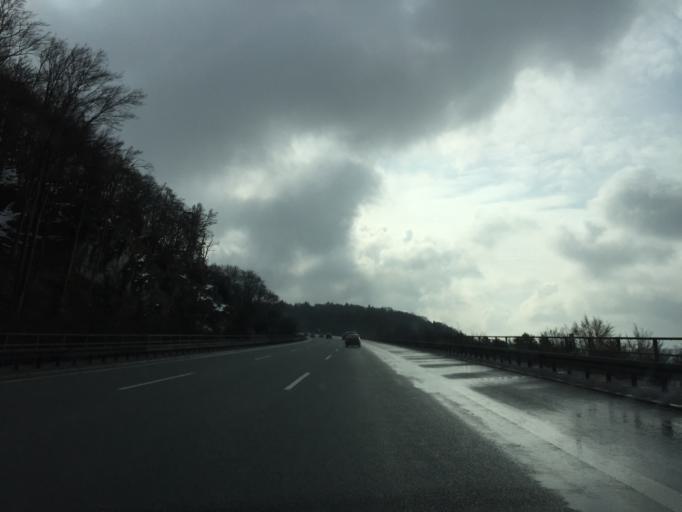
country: DE
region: Bavaria
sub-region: Upper Bavaria
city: Denkendorf
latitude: 48.9742
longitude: 11.3978
